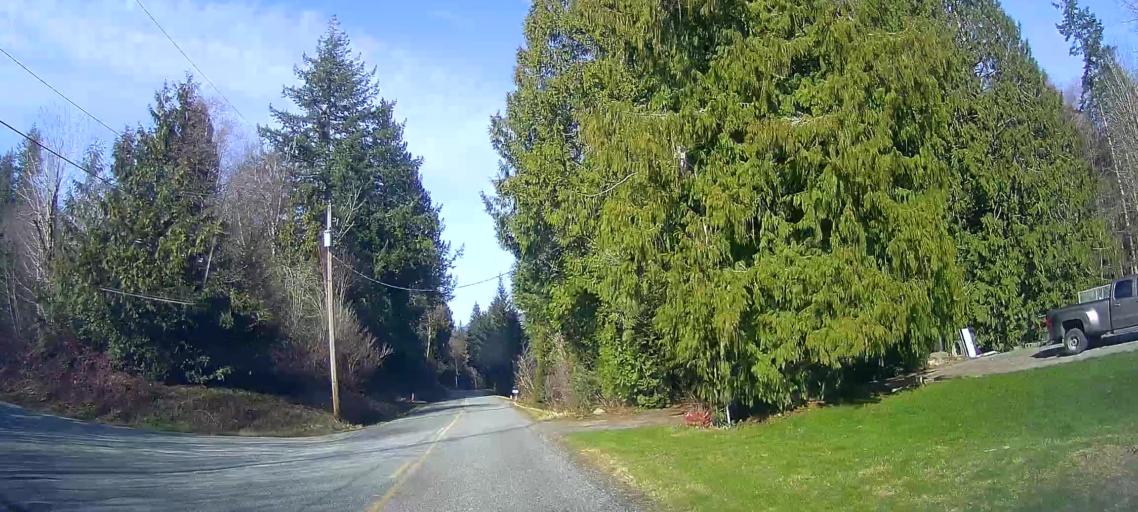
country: US
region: Washington
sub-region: Whatcom County
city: Sudden Valley
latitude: 48.6198
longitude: -122.3692
